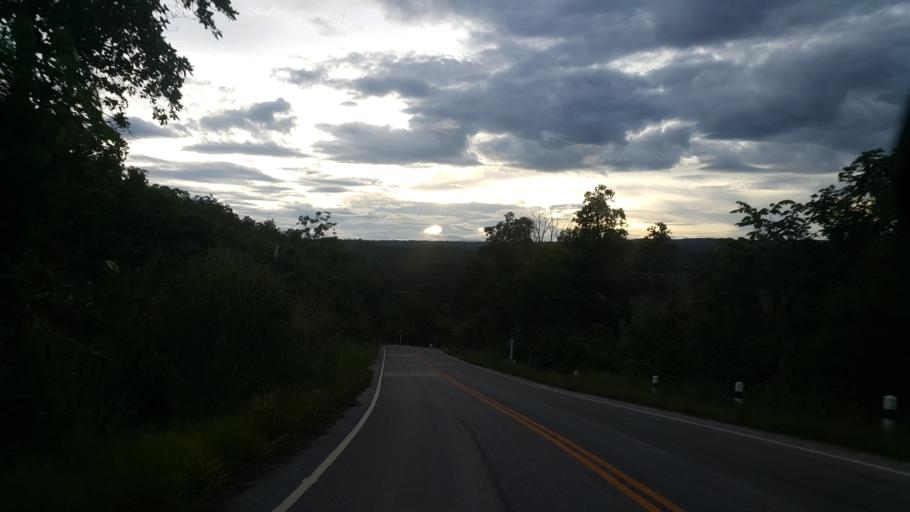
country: TH
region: Loei
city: Na Haeo
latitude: 17.4908
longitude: 101.1748
